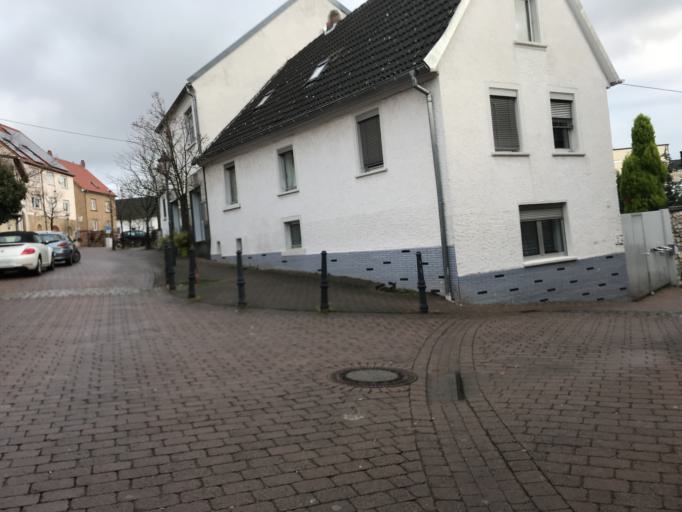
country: DE
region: Rheinland-Pfalz
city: Ober-Olm
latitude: 49.9372
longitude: 8.1930
